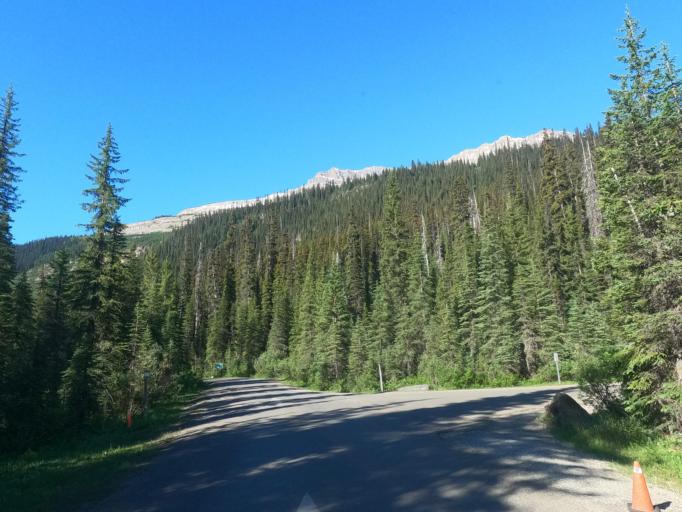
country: CA
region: Alberta
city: Lake Louise
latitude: 51.4984
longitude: -116.4849
